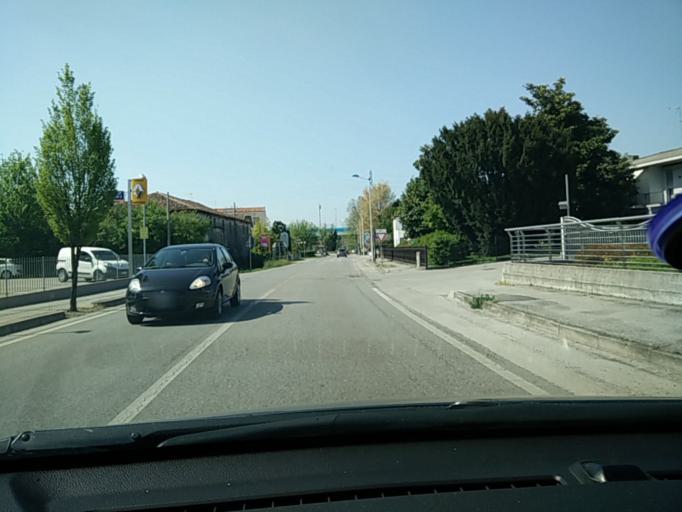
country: IT
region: Veneto
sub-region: Provincia di Treviso
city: Silea
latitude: 45.6555
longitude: 12.2875
